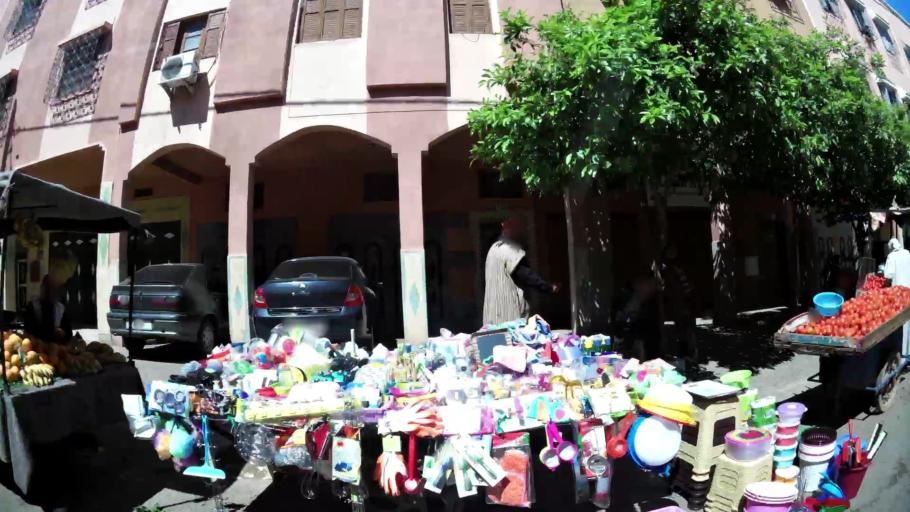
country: MA
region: Marrakech-Tensift-Al Haouz
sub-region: Marrakech
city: Marrakesh
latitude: 31.6333
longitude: -8.0697
